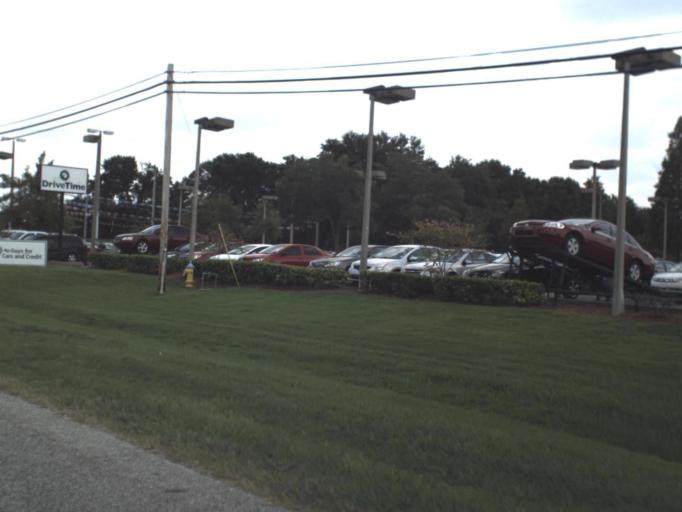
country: US
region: Florida
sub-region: Hillsborough County
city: Palm River-Clair Mel
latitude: 27.9493
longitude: -82.3581
